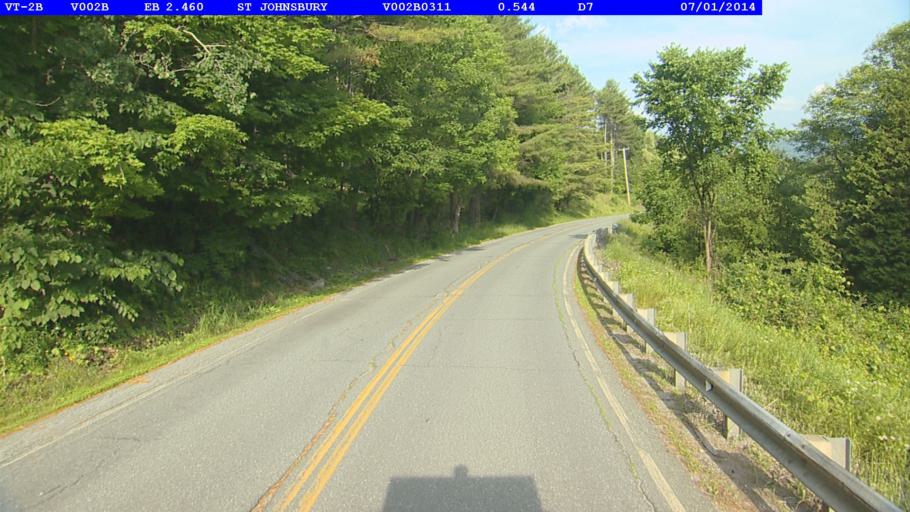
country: US
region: Vermont
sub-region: Caledonia County
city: St Johnsbury
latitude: 44.4273
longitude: -72.0461
